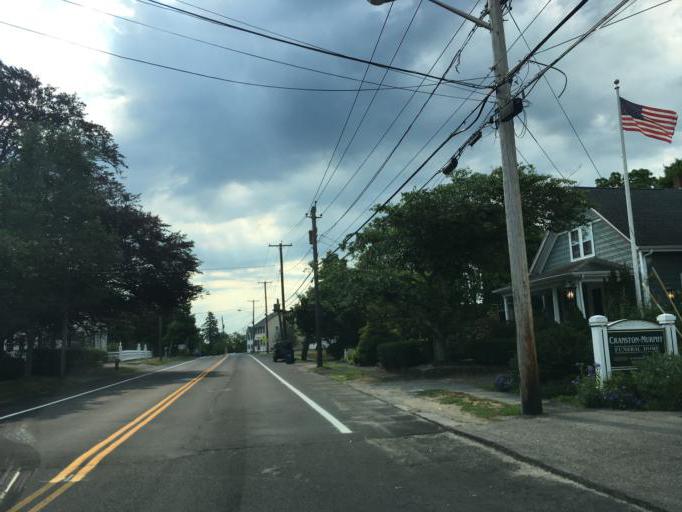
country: US
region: Rhode Island
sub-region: Washington County
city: North Kingstown
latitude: 41.5719
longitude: -71.4571
